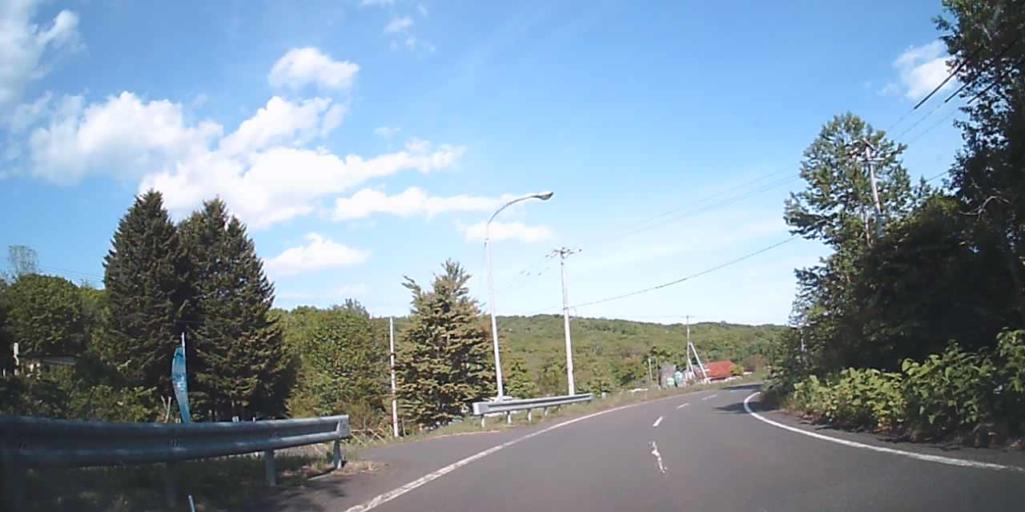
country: JP
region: Hokkaido
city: Tomakomai
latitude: 42.6398
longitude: 141.4814
